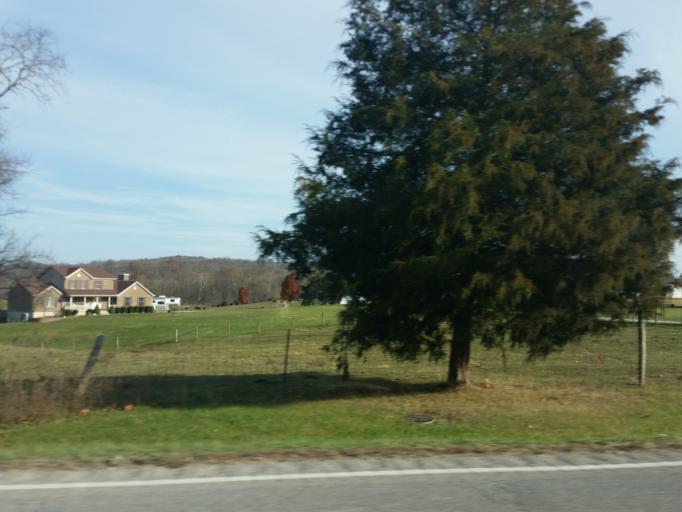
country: US
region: Kentucky
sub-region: Pendleton County
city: Falmouth
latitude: 38.7670
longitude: -84.3529
